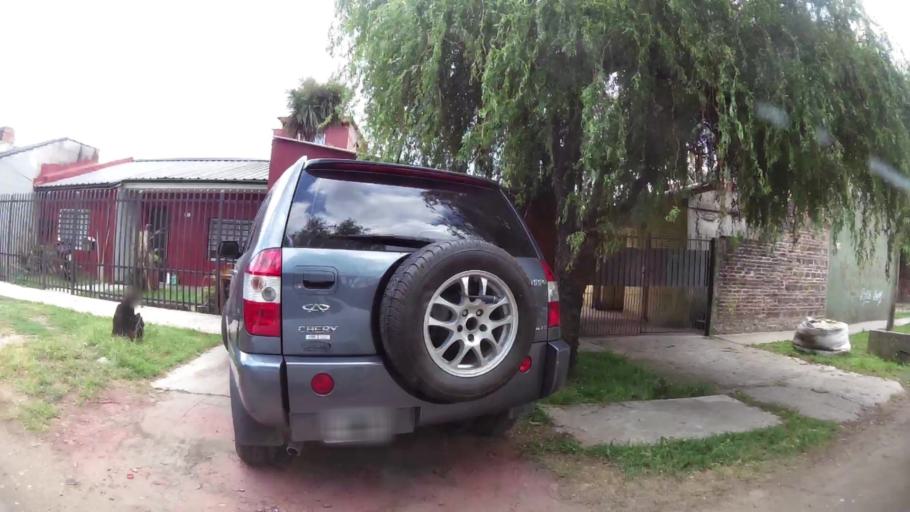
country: AR
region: Buenos Aires
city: Ituzaingo
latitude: -34.6379
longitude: -58.6726
